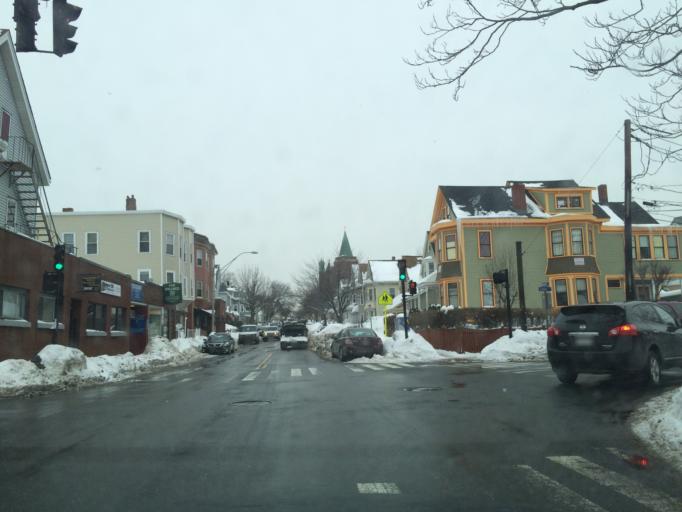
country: US
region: Massachusetts
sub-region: Middlesex County
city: Somerville
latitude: 42.3890
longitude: -71.0971
